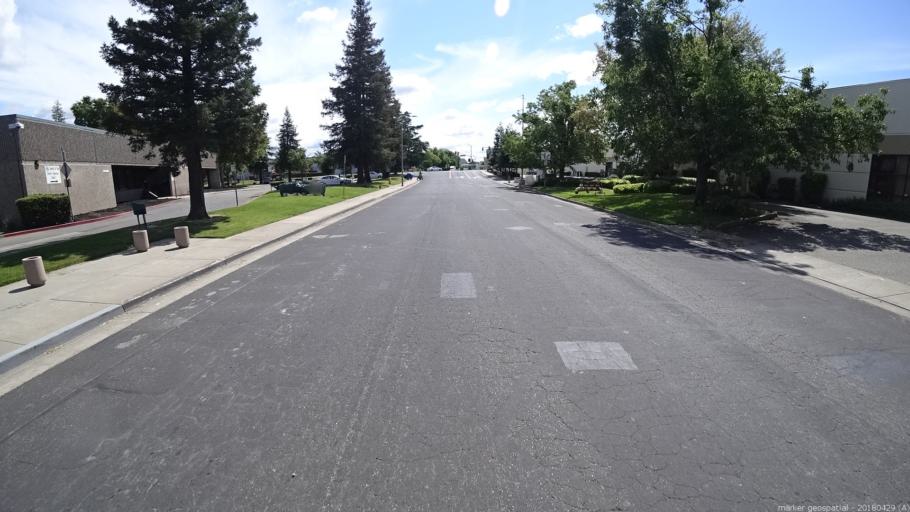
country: US
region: California
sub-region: Yolo County
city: West Sacramento
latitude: 38.5871
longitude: -121.5282
